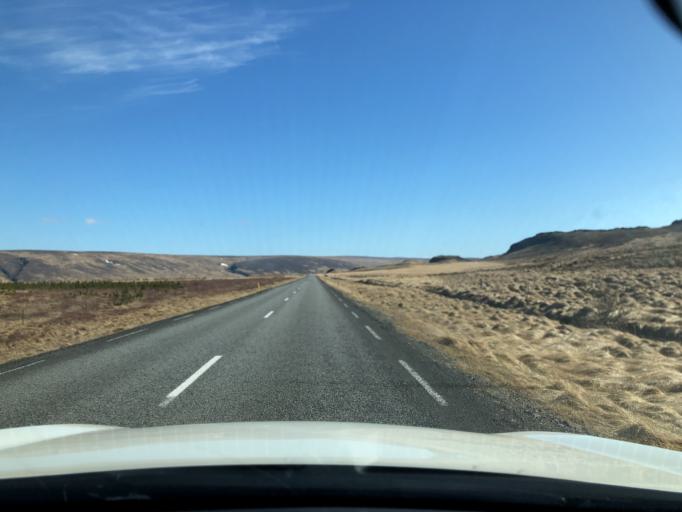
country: IS
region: Capital Region
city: Mosfellsbaer
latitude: 64.6773
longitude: -21.2526
